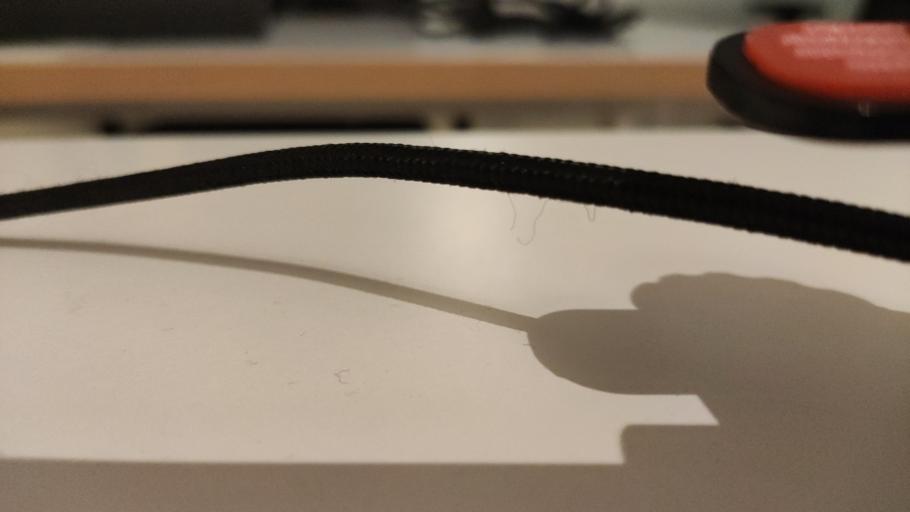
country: RU
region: Moskovskaya
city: Mikhnevo
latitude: 55.0800
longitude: 37.9606
